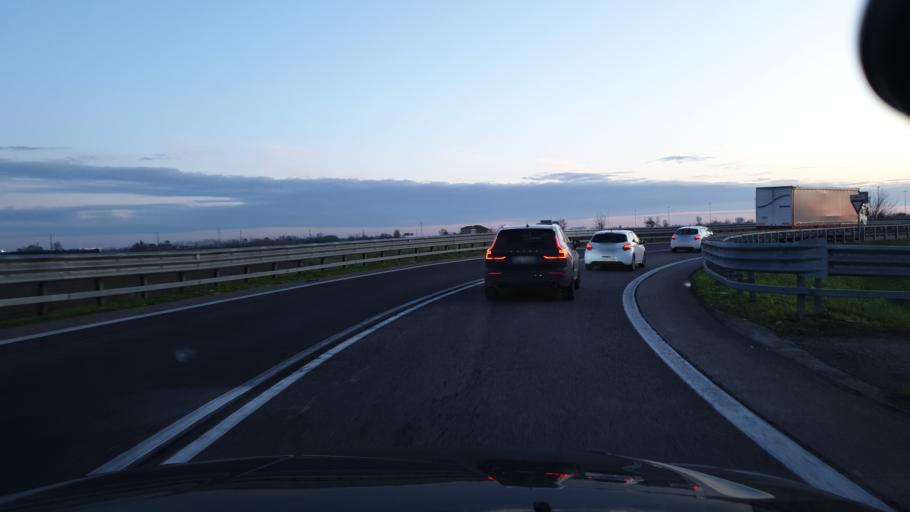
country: IT
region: Veneto
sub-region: Provincia di Rovigo
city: Villamarzana
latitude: 45.0248
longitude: 11.6941
